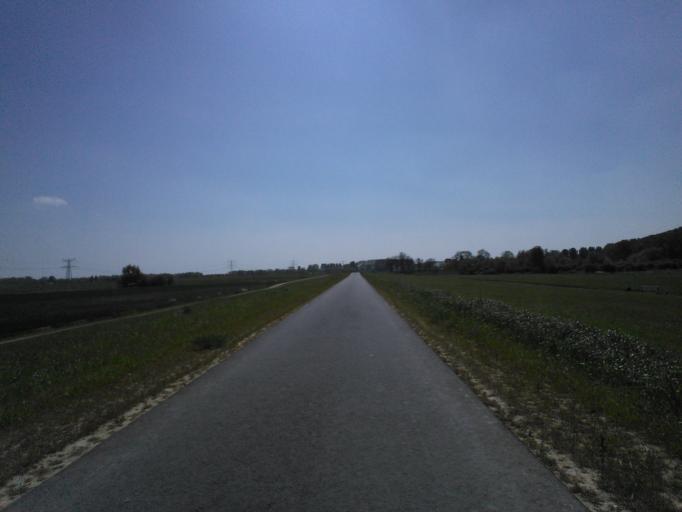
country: NL
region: South Holland
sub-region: Gemeente Sliedrecht
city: Sliedrecht
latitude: 51.8007
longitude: 4.7394
